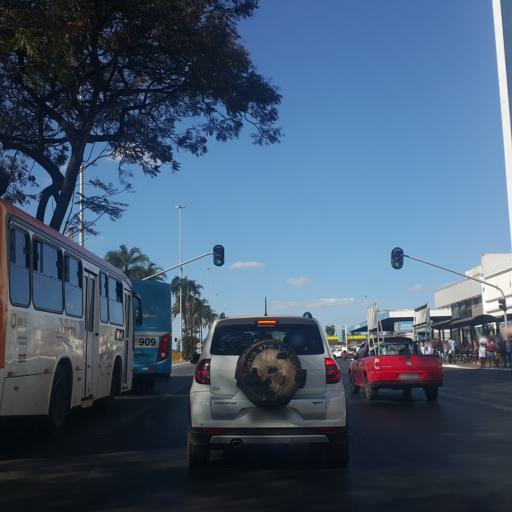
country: BR
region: Federal District
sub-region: Brasilia
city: Brasilia
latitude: -15.8332
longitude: -48.0550
